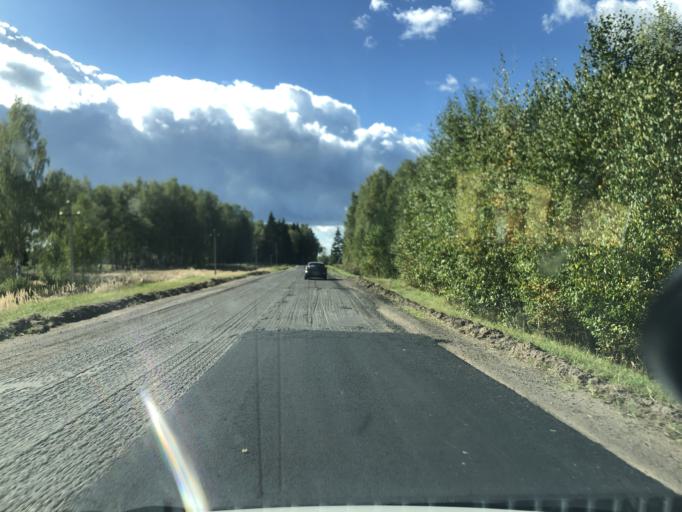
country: RU
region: Jaroslavl
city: Porech'ye-Rybnoye
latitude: 56.9719
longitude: 39.4000
